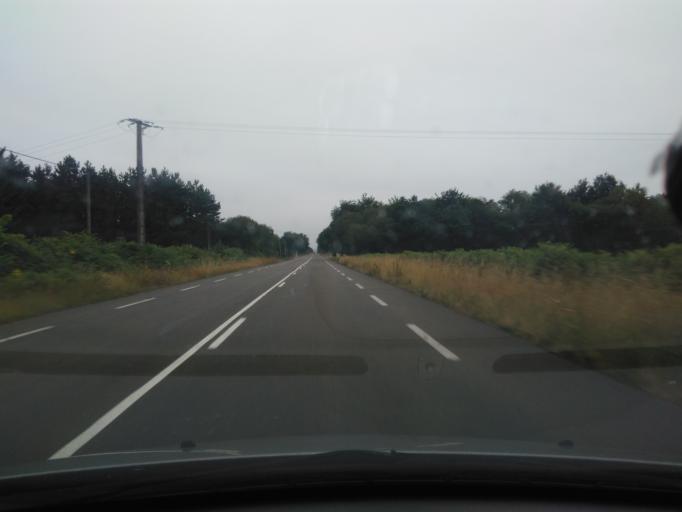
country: FR
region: Pays de la Loire
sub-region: Departement de la Vendee
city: Saint-Georges-de-Pointindoux
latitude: 46.6290
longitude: -1.6176
